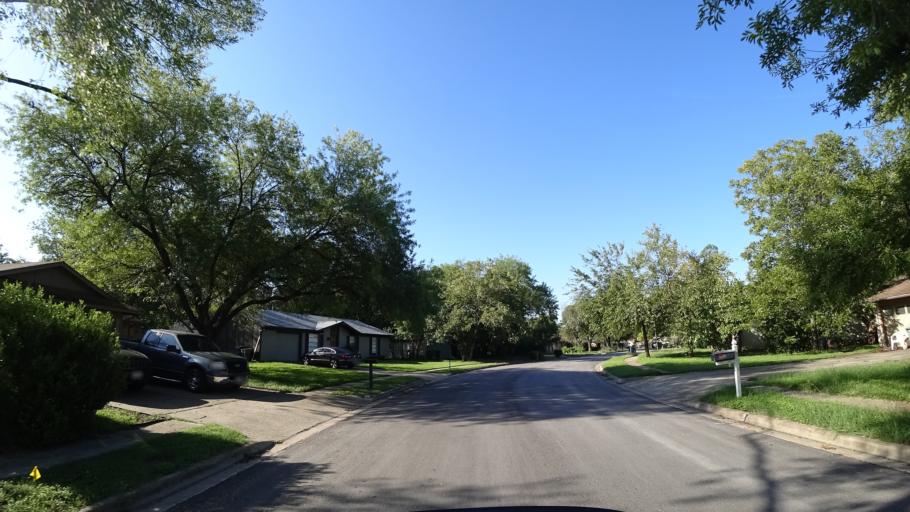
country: US
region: Texas
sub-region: Travis County
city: Shady Hollow
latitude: 30.2077
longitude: -97.8101
